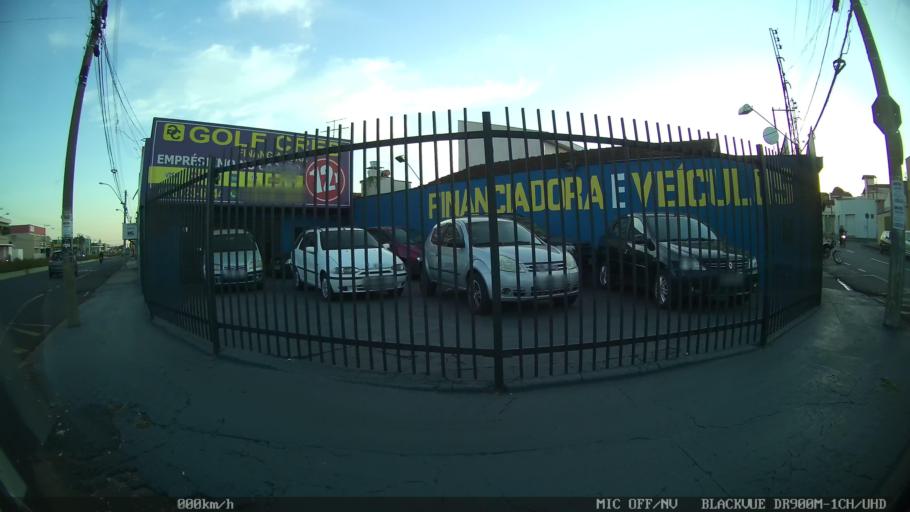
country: BR
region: Sao Paulo
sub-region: Franca
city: Franca
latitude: -20.5263
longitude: -47.4020
